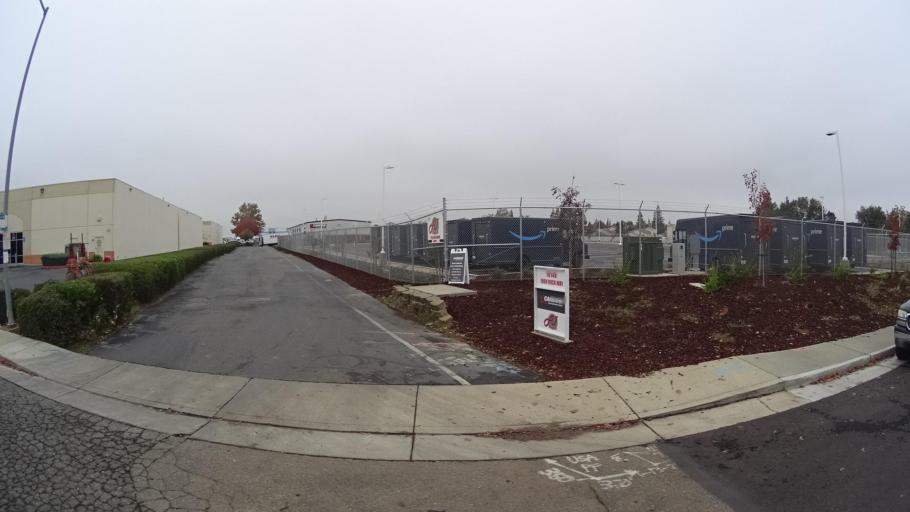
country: US
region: California
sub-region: Sacramento County
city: Elk Grove
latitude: 38.3896
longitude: -121.3603
